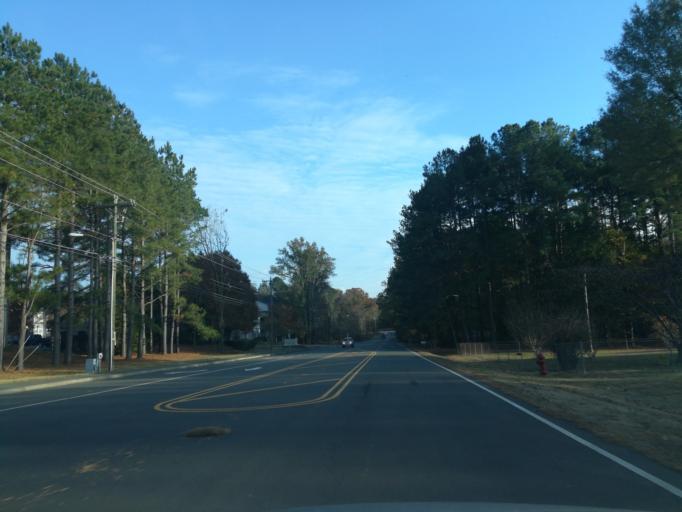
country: US
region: North Carolina
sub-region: Orange County
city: Chapel Hill
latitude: 35.9604
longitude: -78.9984
